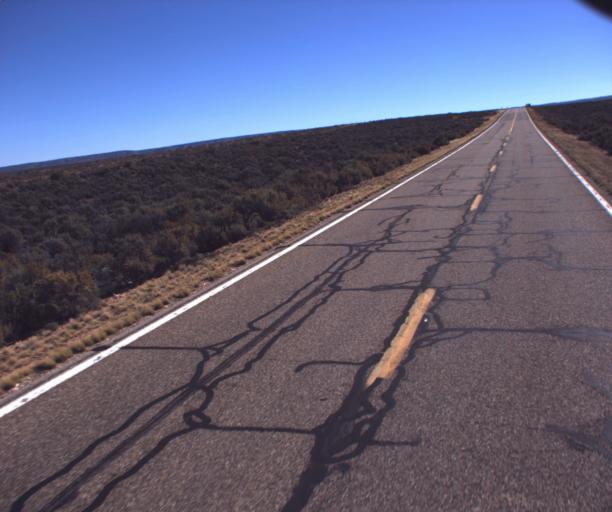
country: US
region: Arizona
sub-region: Coconino County
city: Fredonia
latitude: 36.8943
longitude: -112.3623
